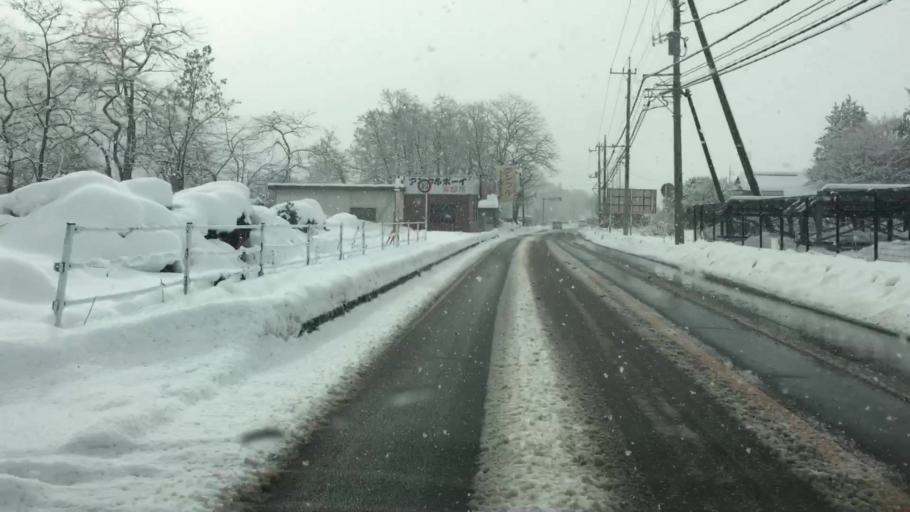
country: JP
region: Gunma
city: Numata
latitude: 36.7094
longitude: 139.0662
